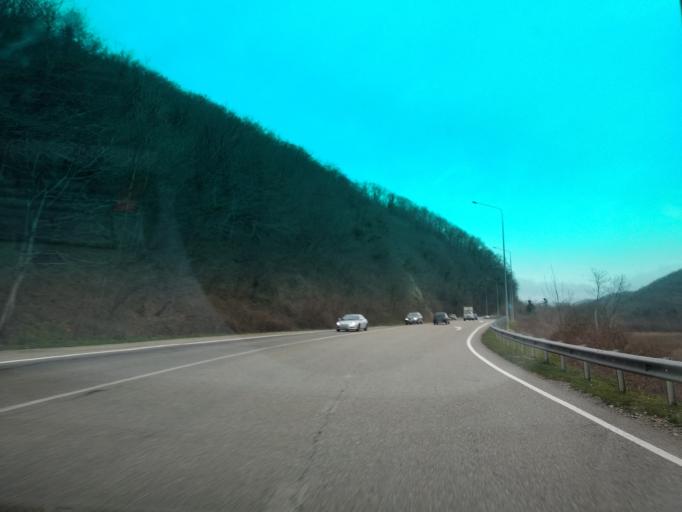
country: RU
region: Krasnodarskiy
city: Ol'ginka
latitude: 44.2184
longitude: 38.8941
